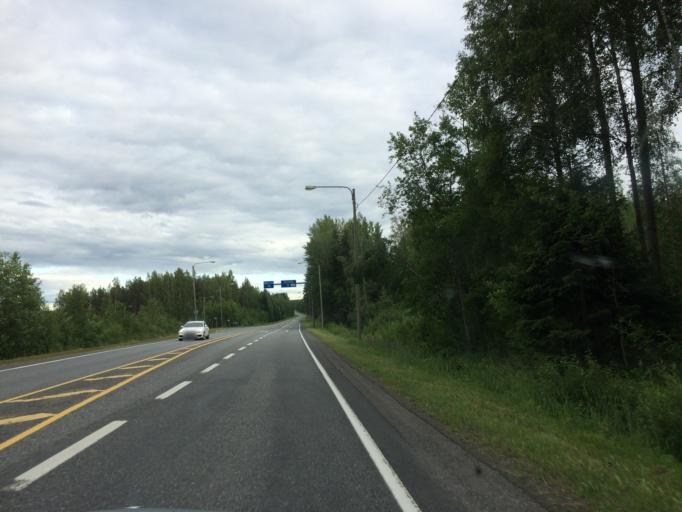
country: FI
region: Haeme
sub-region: Haemeenlinna
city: Haemeenlinna
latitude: 60.9427
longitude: 24.5180
